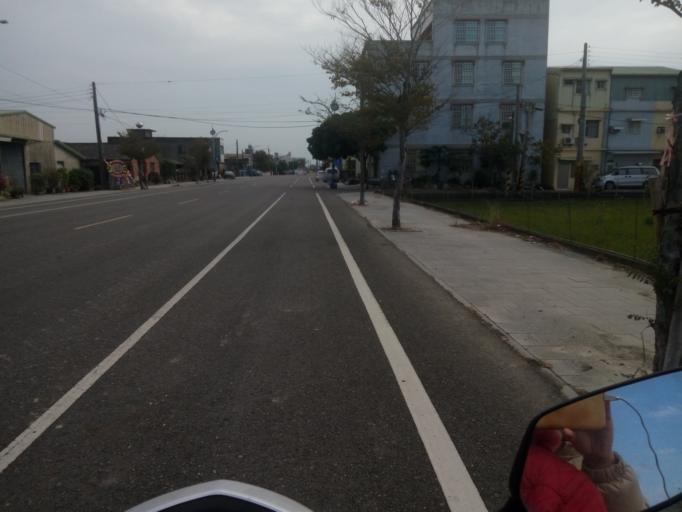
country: TW
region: Taiwan
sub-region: Chiayi
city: Taibao
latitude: 23.4835
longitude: 120.3351
